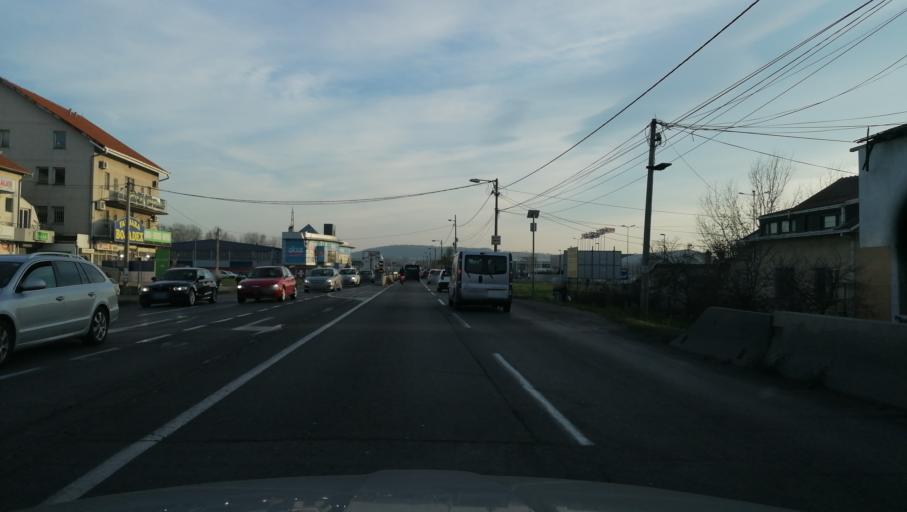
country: RS
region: Central Serbia
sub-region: Belgrade
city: Stari Grad
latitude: 44.8443
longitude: 20.4892
